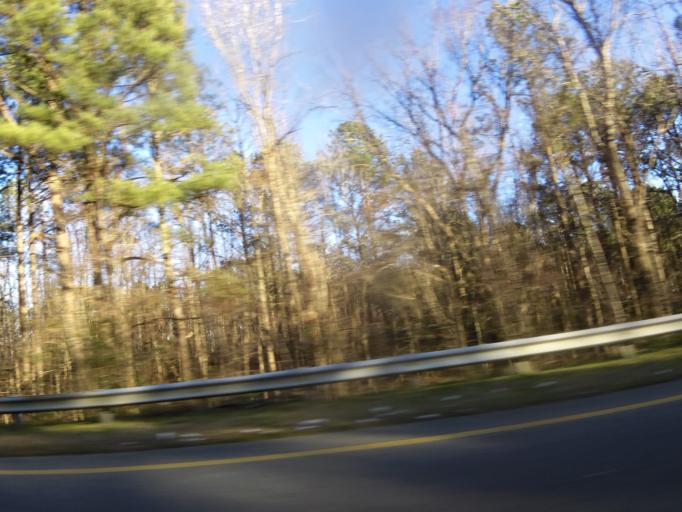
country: US
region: Virginia
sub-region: Isle of Wight County
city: Windsor
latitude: 36.6808
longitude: -76.7730
